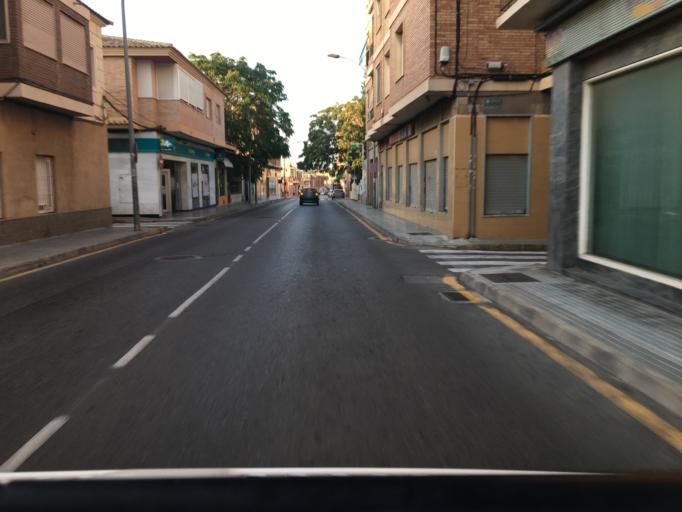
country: ES
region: Murcia
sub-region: Murcia
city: Cartagena
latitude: 37.6221
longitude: -0.9888
